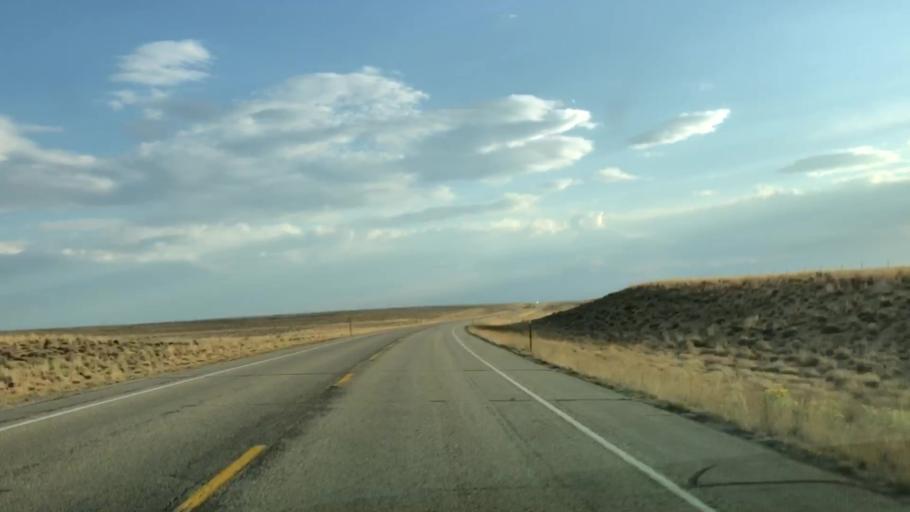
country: US
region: Wyoming
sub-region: Sweetwater County
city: North Rock Springs
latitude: 42.2166
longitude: -109.4699
